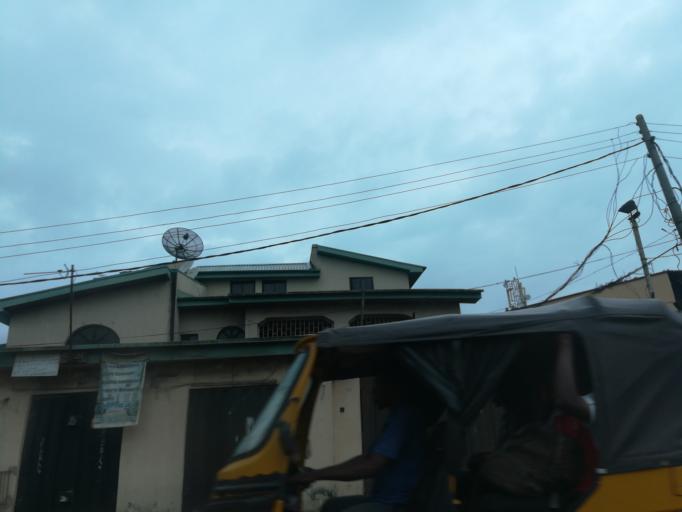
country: NG
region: Lagos
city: Oshodi
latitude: 6.5683
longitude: 3.3419
